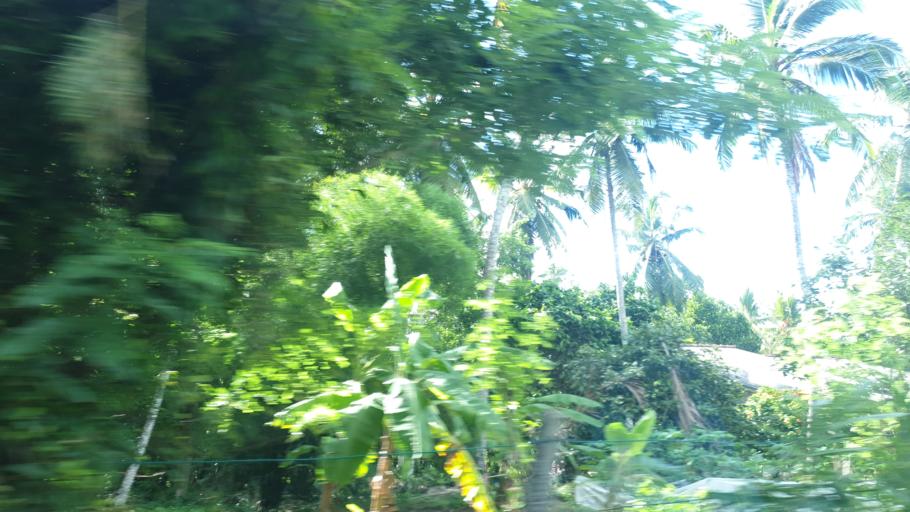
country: LK
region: Western
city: Kandana
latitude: 7.0596
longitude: 79.9303
